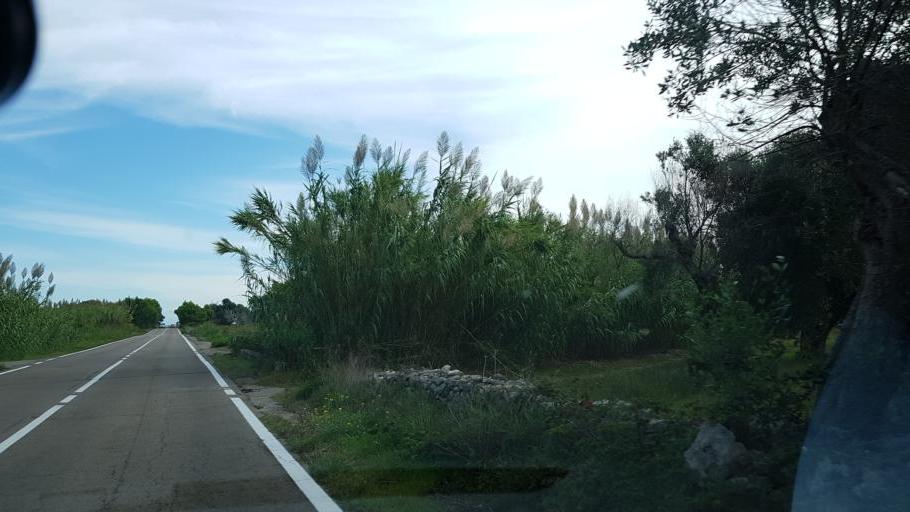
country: IT
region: Apulia
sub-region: Provincia di Lecce
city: Melendugno
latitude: 40.3370
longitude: 18.3515
